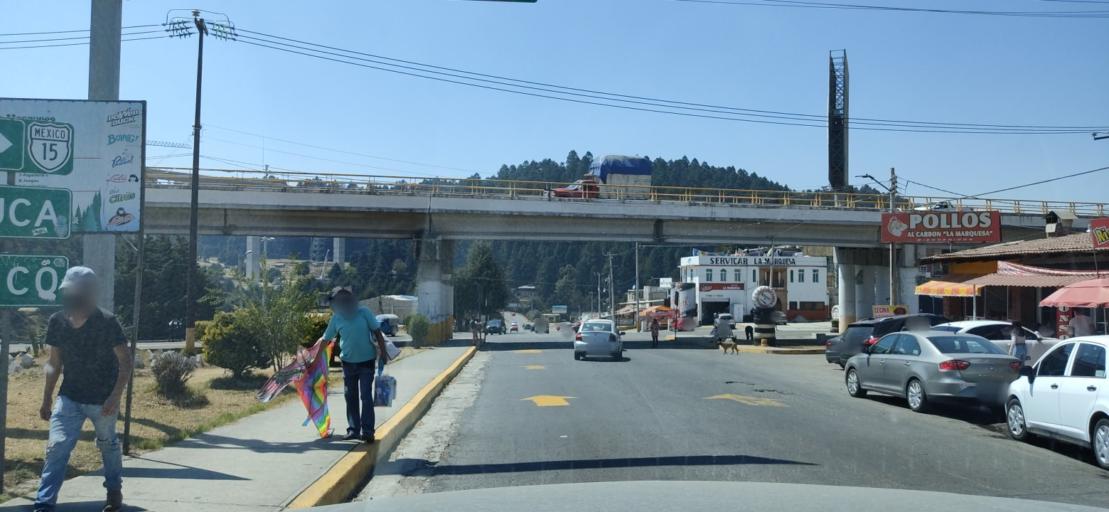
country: MX
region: Mexico
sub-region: Huixquilucan
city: El Palacio
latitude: 19.2987
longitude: -99.3721
